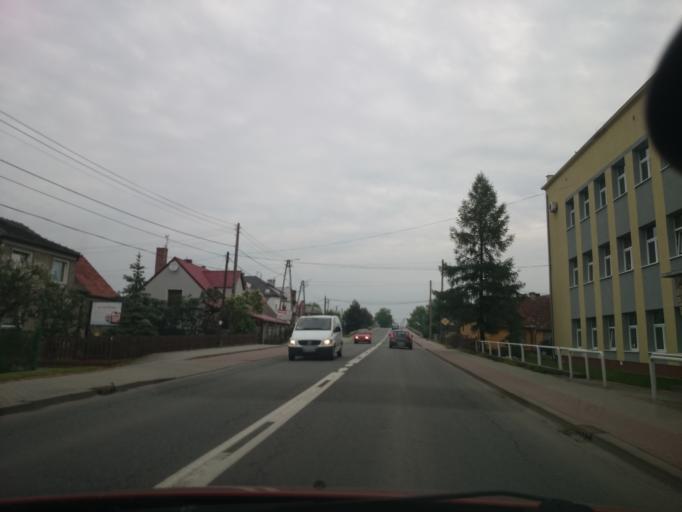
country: PL
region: Opole Voivodeship
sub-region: Powiat opolski
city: Dobrzen Wielki
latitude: 50.7732
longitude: 17.8552
